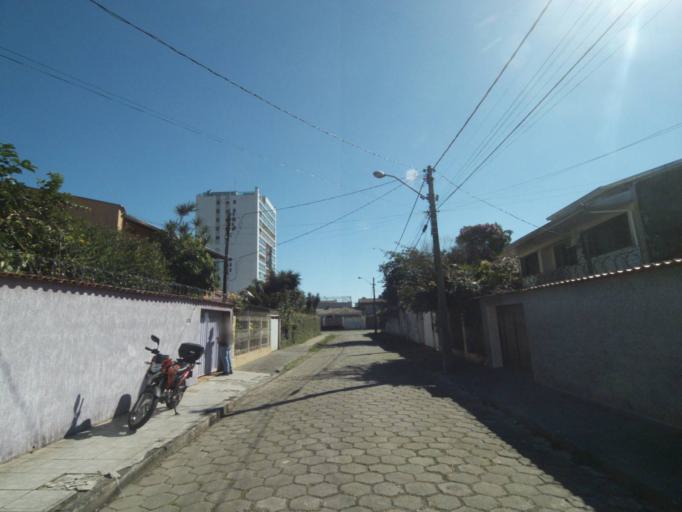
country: BR
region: Parana
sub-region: Paranagua
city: Paranagua
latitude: -25.5145
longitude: -48.5024
